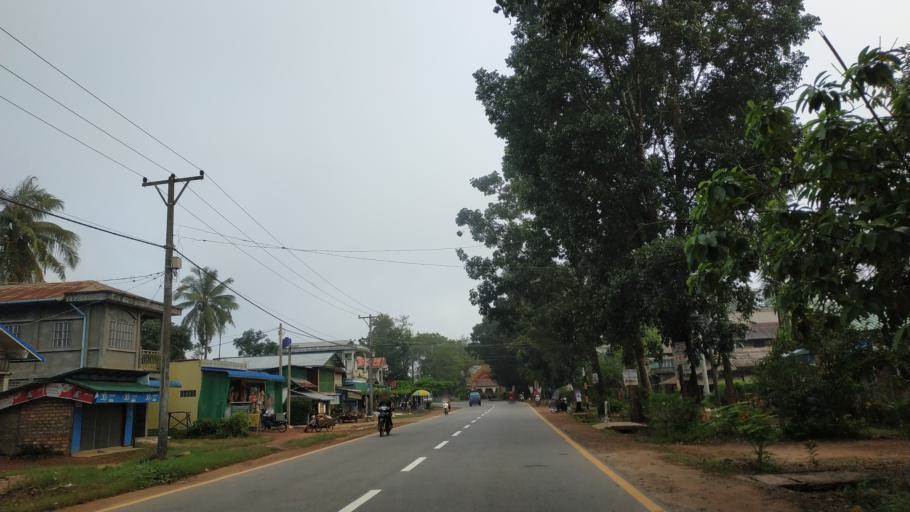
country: MM
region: Tanintharyi
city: Dawei
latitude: 14.1305
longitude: 98.2161
